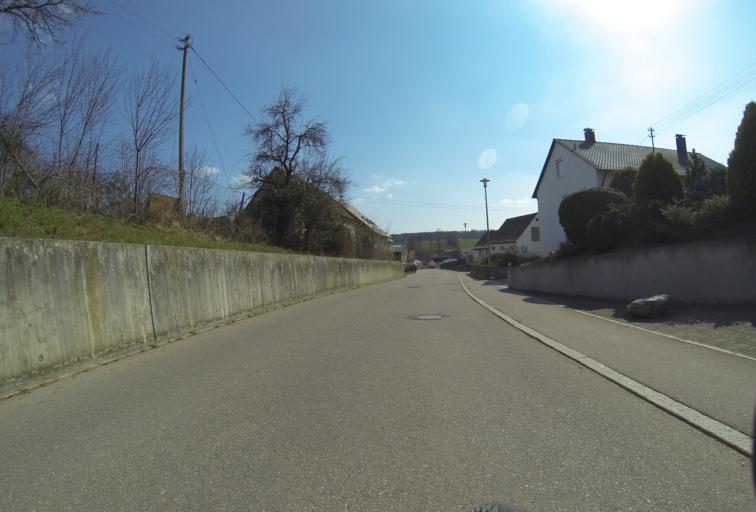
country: DE
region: Baden-Wuerttemberg
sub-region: Tuebingen Region
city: Huttisheim
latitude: 48.2625
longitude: 9.9583
